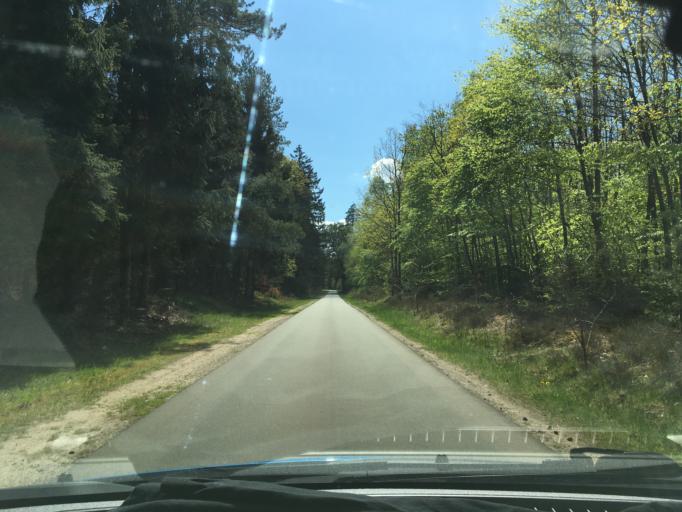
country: DE
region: Lower Saxony
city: Stoetze
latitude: 53.1085
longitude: 10.7848
